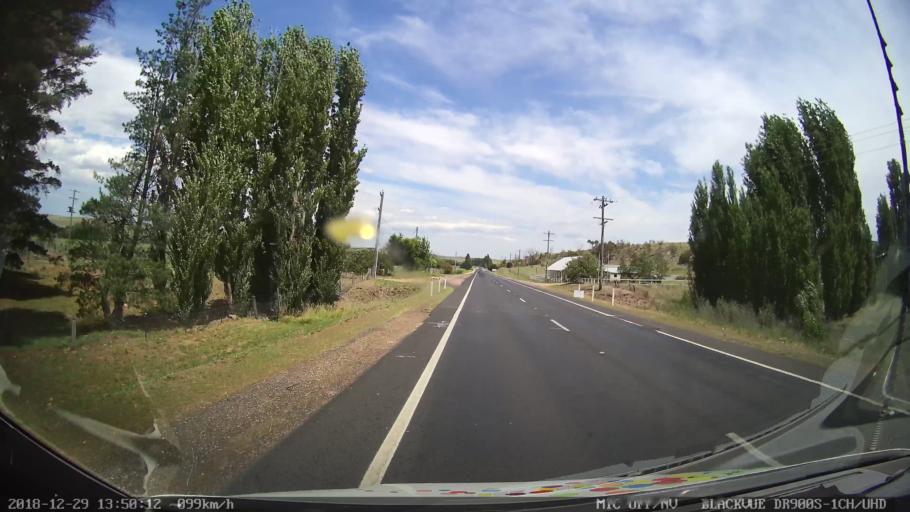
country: AU
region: New South Wales
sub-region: Cooma-Monaro
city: Cooma
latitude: -36.1646
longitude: 149.1533
